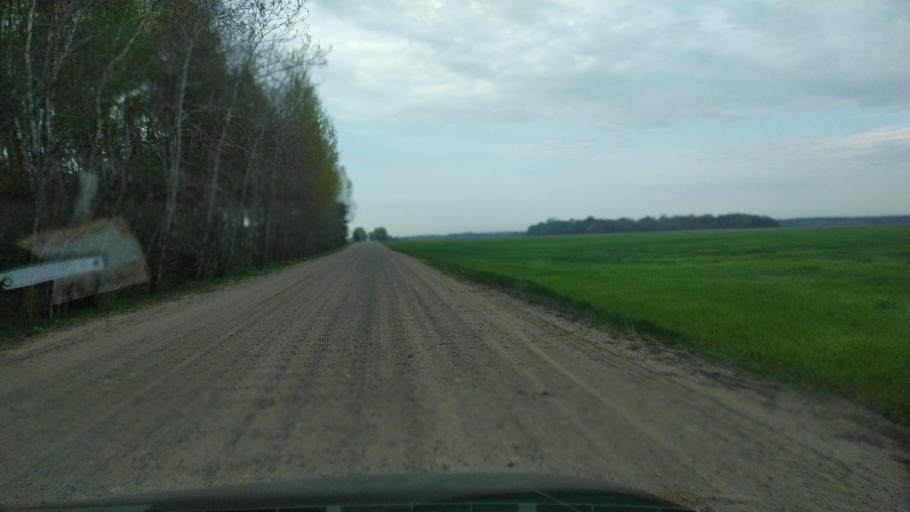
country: BY
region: Brest
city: Zhabinka
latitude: 52.1480
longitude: 24.0951
